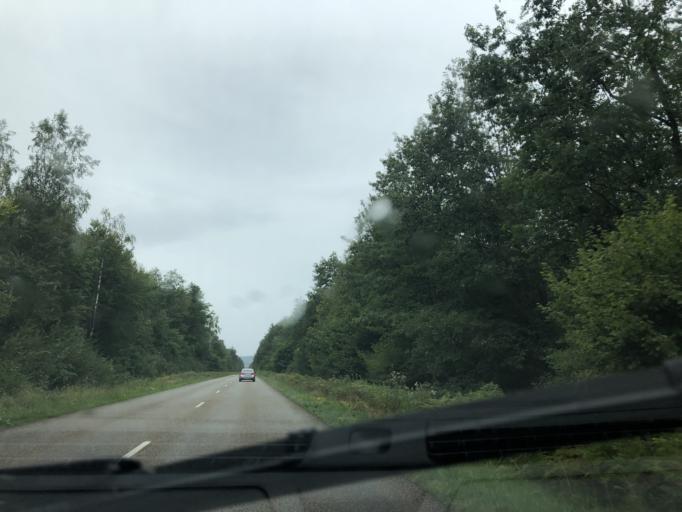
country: DE
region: Rheinland-Pfalz
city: Kapsweyer
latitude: 49.0168
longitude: 8.0162
